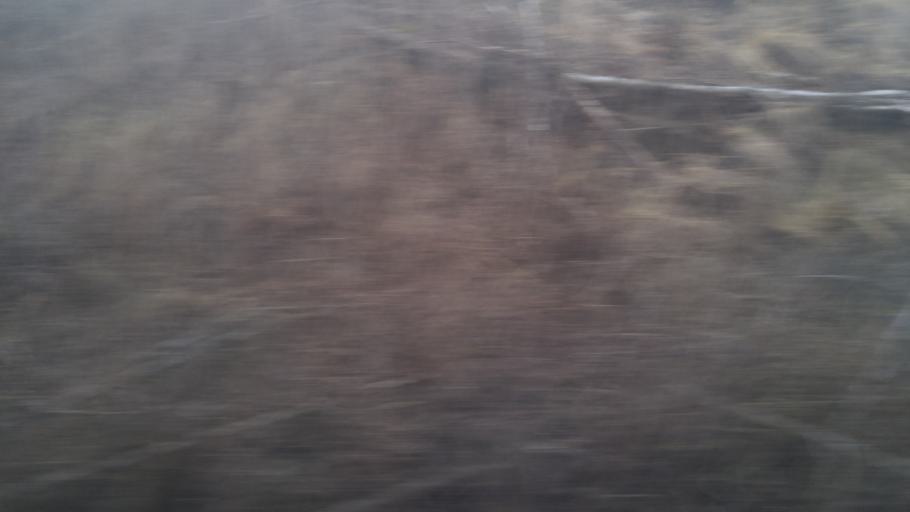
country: NO
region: Akershus
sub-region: Eidsvoll
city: Eidsvoll
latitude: 60.3641
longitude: 11.2451
